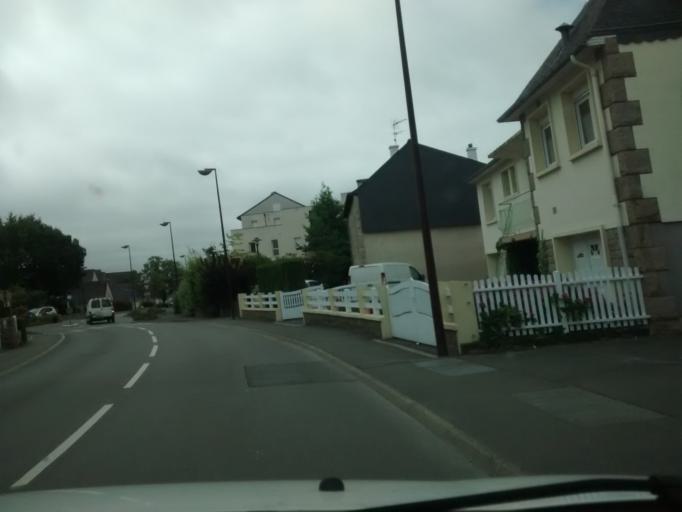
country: FR
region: Brittany
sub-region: Departement d'Ille-et-Vilaine
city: Chantepie
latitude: 48.0935
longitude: -1.6183
